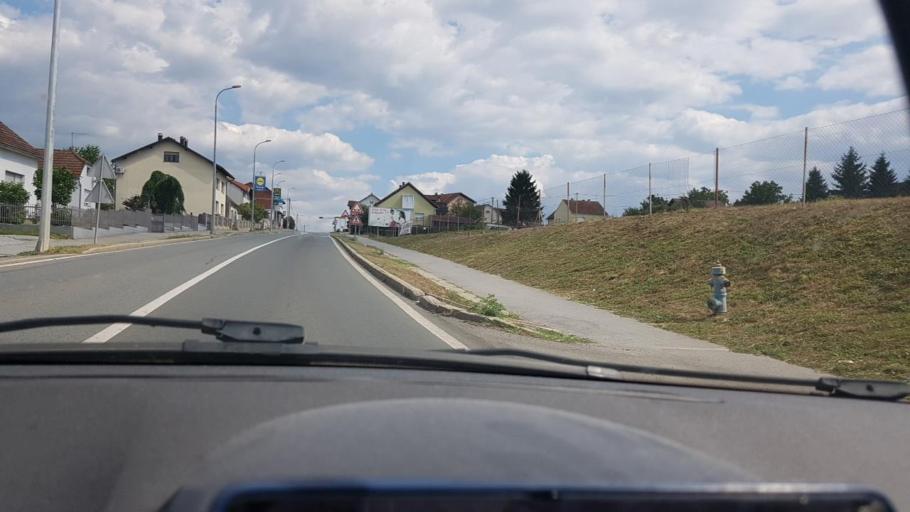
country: HR
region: Bjelovarsko-Bilogorska
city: Bjelovar
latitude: 45.8895
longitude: 16.8584
